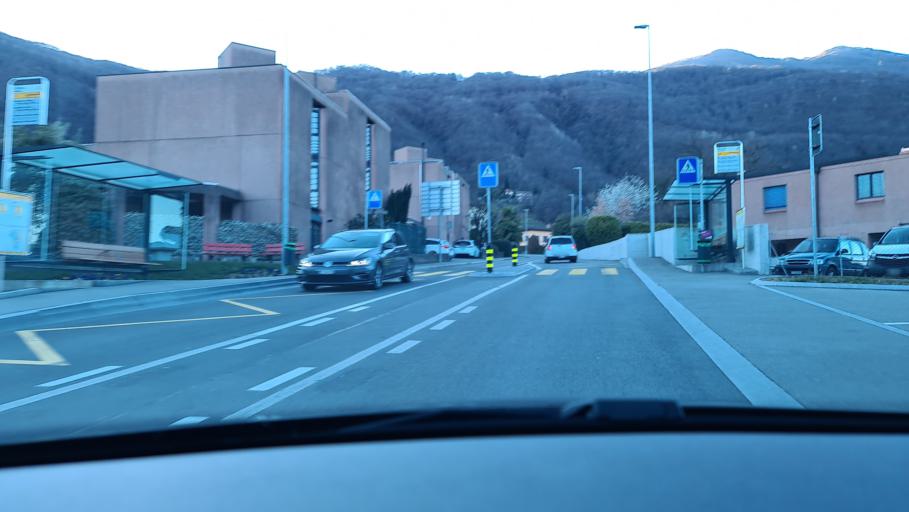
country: CH
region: Ticino
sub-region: Lugano District
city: Gravesano
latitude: 46.0411
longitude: 8.9231
